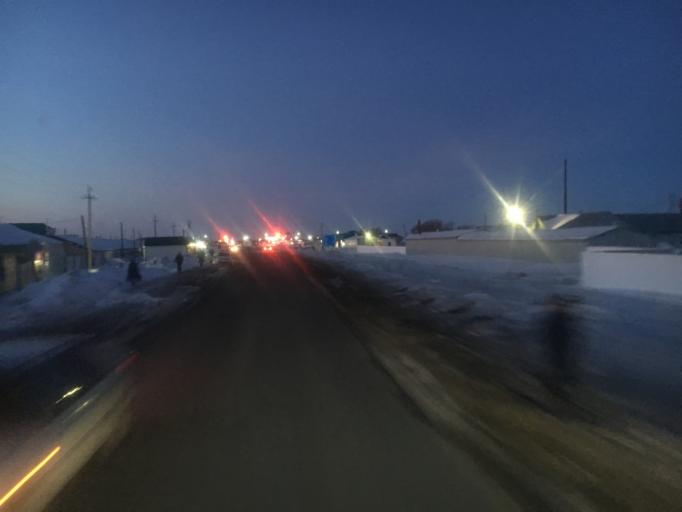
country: KZ
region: Batys Qazaqstan
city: Oral
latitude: 51.1518
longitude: 51.4892
